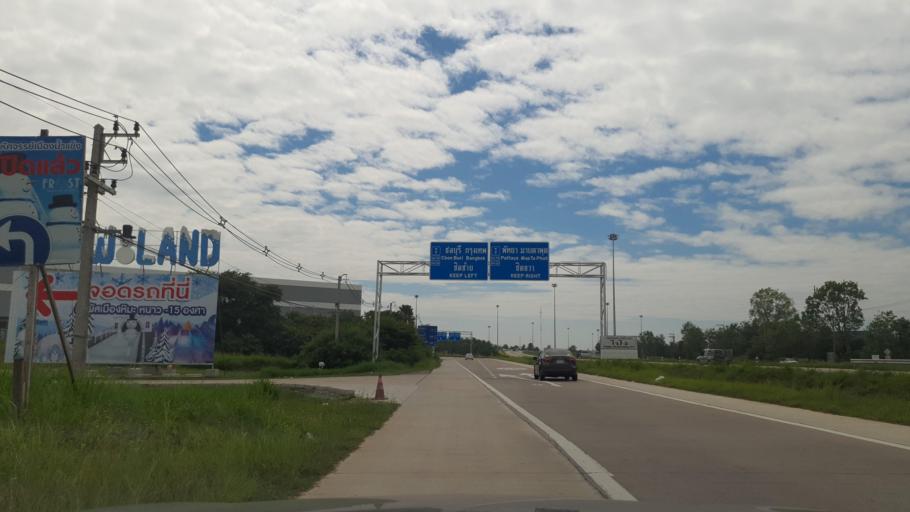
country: TH
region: Chon Buri
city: Bang Lamung
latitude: 12.9691
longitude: 100.9754
